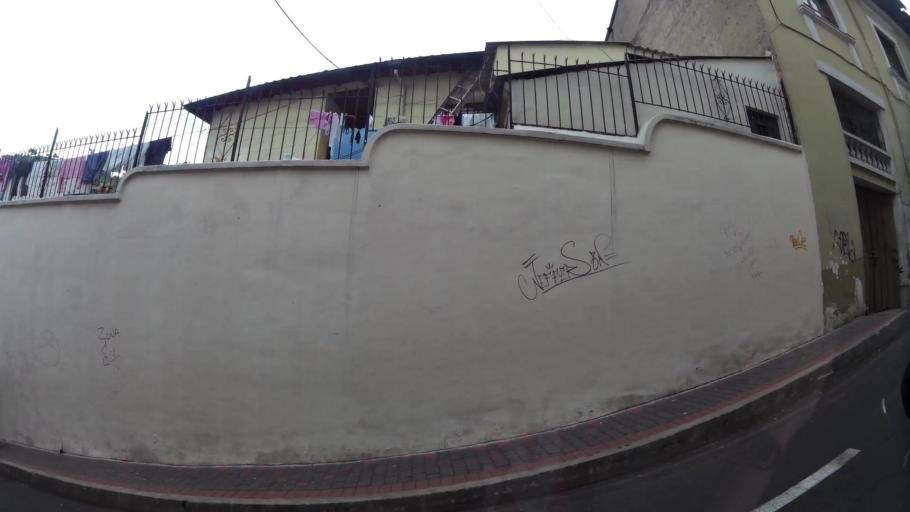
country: EC
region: Pichincha
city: Quito
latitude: -0.2282
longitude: -78.5108
